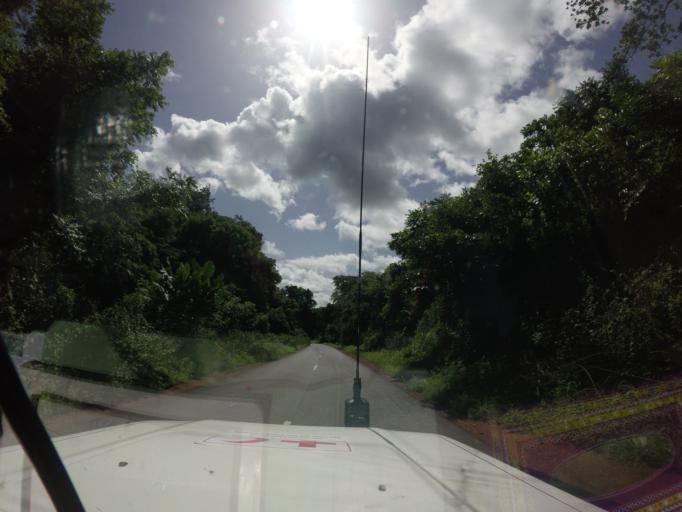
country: GN
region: Mamou
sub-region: Mamou Prefecture
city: Mamou
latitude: 10.2347
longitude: -11.8692
